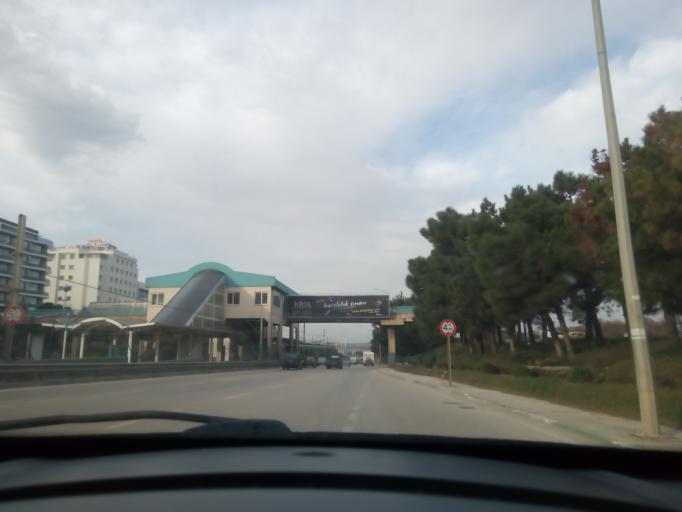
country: TR
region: Bursa
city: Cali
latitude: 40.2128
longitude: 28.9508
